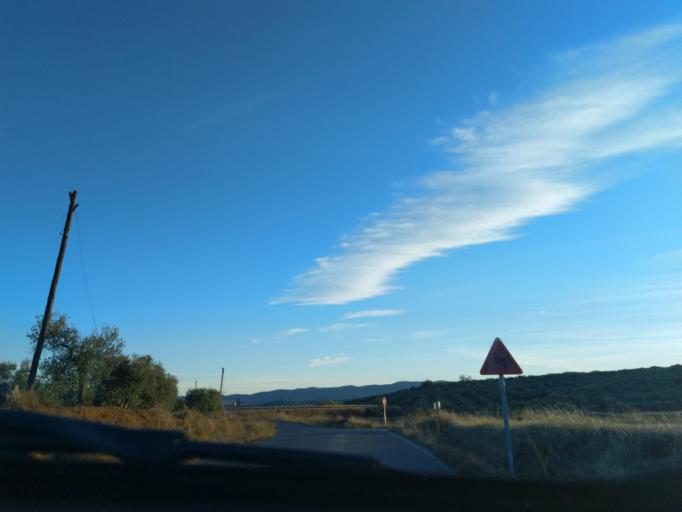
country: ES
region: Extremadura
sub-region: Provincia de Badajoz
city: Valverde de Llerena
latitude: 38.2235
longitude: -5.8229
